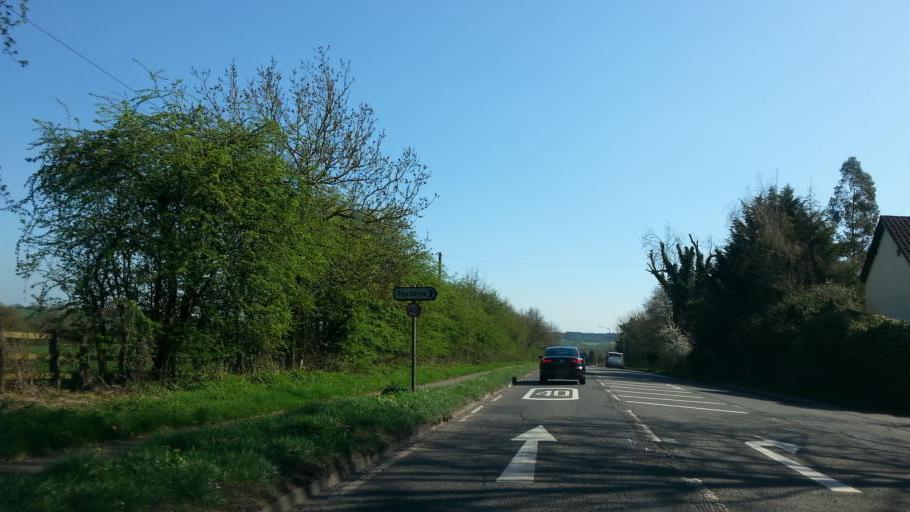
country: GB
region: England
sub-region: Worcestershire
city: Alvechurch
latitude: 52.3745
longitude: -1.9576
